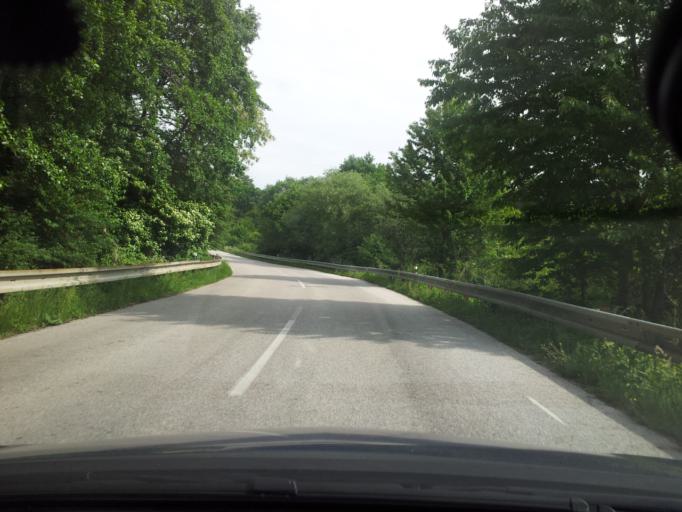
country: SK
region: Nitriansky
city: Zlate Moravce
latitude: 48.5071
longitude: 18.4331
